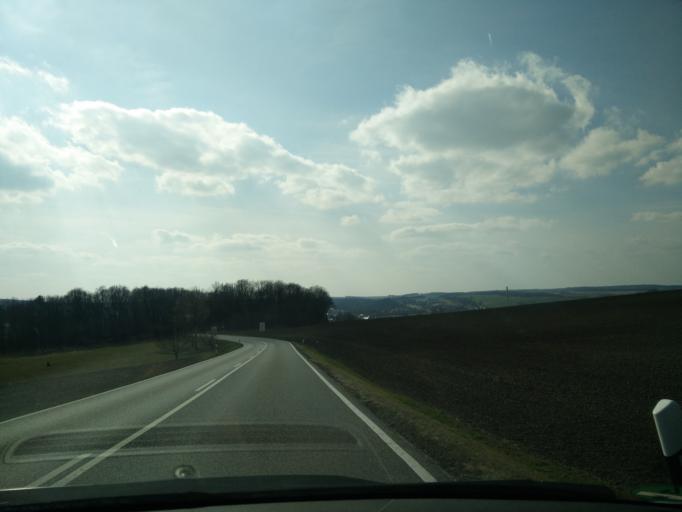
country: DE
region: Saxony
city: Zettlitz
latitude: 51.0546
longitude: 12.8180
